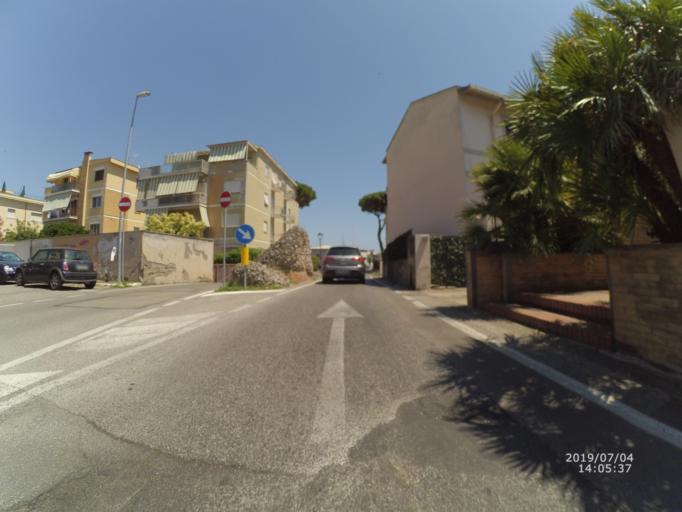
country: IT
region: Latium
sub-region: Provincia di Latina
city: Terracina
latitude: 41.2847
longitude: 13.2519
